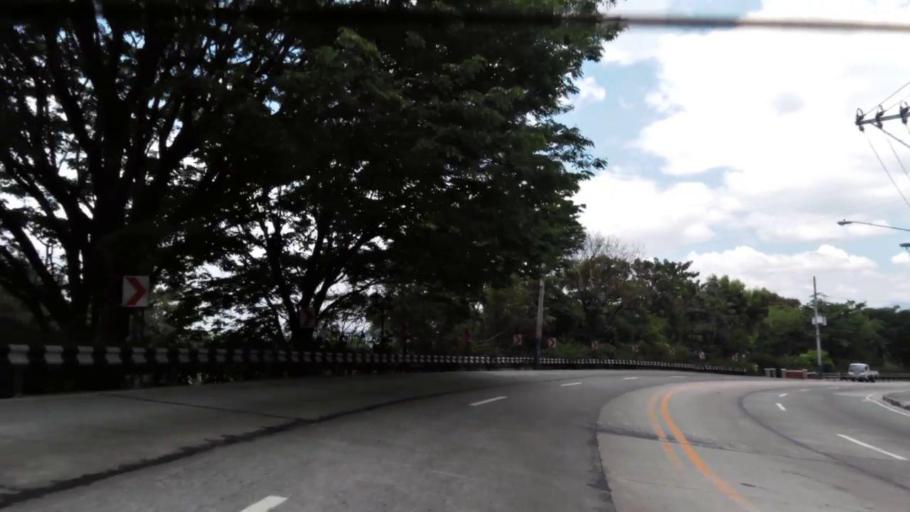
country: PH
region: Calabarzon
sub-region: Province of Rizal
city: Antipolo
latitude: 14.6151
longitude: 121.1512
